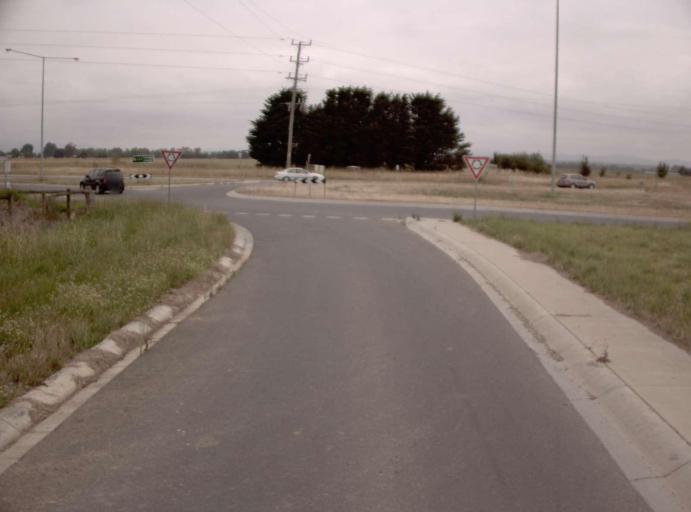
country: AU
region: Victoria
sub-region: Wellington
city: Heyfield
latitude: -38.0226
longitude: 146.7651
